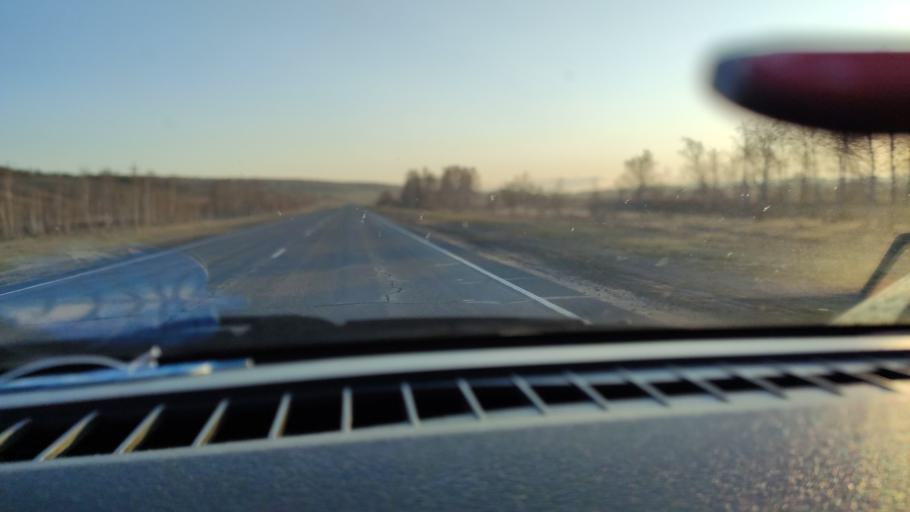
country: RU
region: Saratov
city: Sinodskoye
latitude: 52.0603
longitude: 46.7631
